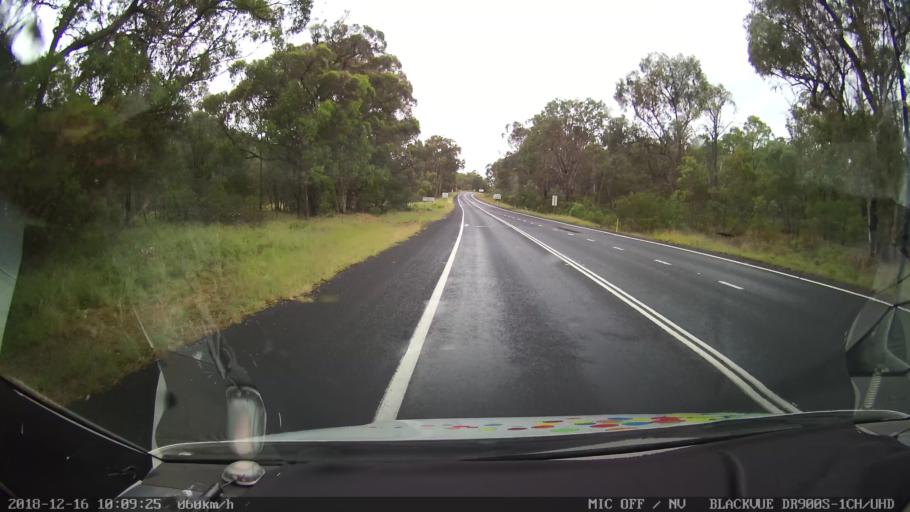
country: AU
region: New South Wales
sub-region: Glen Innes Severn
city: Glen Innes
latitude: -29.3241
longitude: 151.9162
